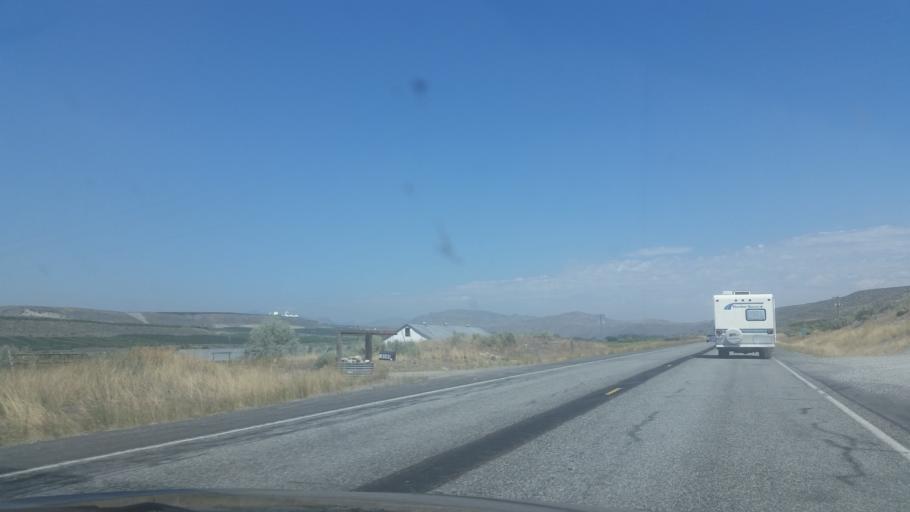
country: US
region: Washington
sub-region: Okanogan County
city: Brewster
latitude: 48.1133
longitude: -119.6797
